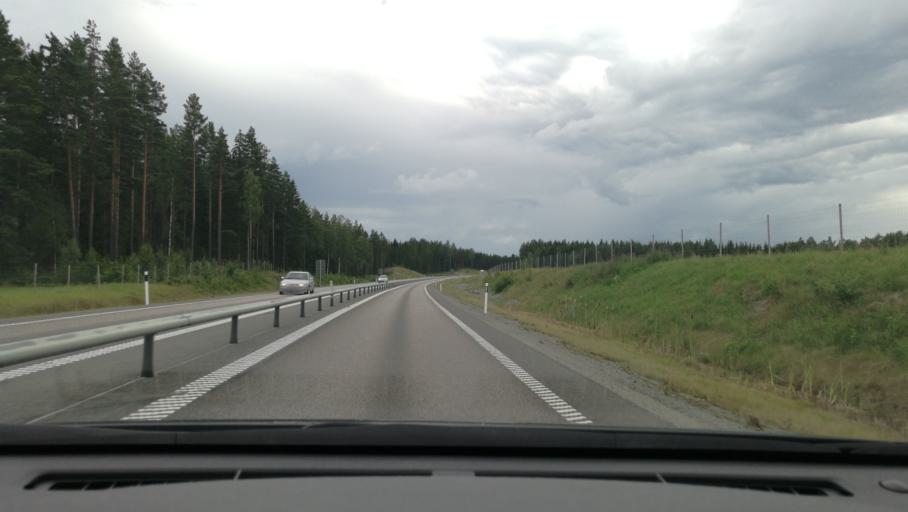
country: SE
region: Soedermanland
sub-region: Katrineholms Kommun
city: Katrineholm
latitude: 58.9839
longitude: 16.2661
